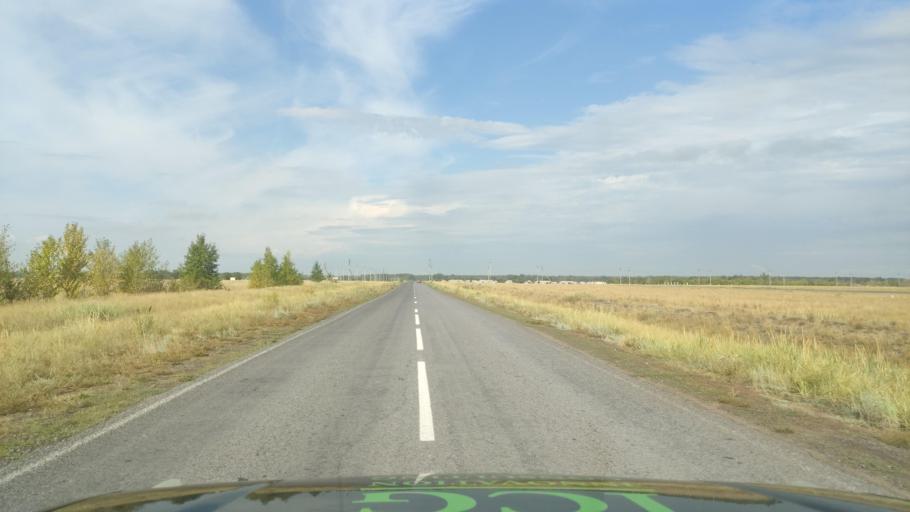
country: KZ
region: Pavlodar
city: Leninskiy
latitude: 52.4779
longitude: 76.8358
